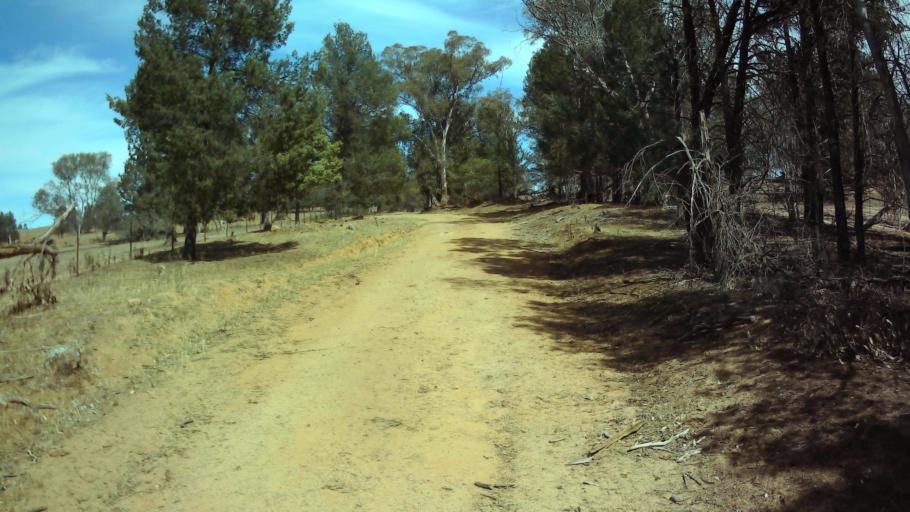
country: AU
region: New South Wales
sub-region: Weddin
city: Grenfell
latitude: -33.6797
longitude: 148.2635
